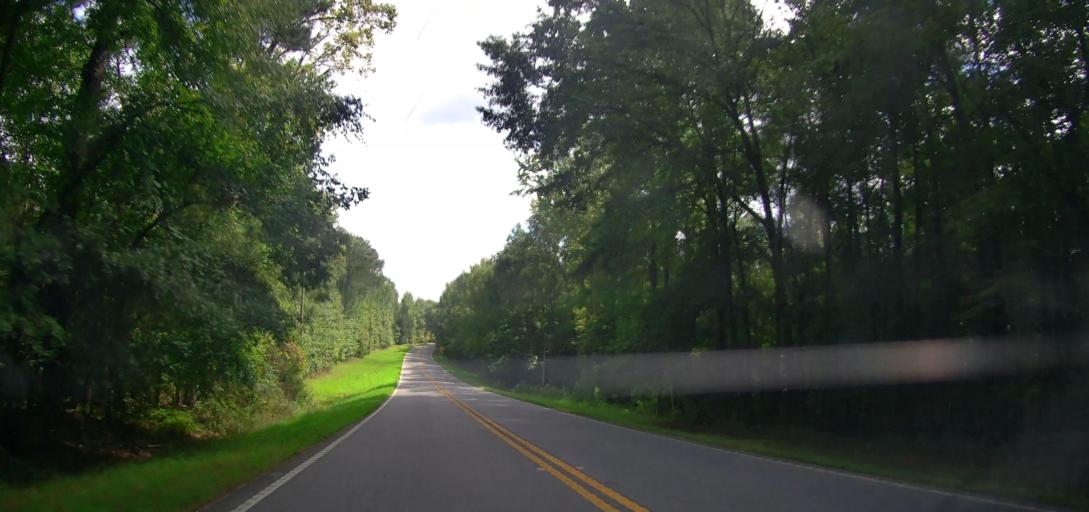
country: US
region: Georgia
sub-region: Talbot County
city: Talbotton
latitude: 32.6286
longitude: -84.4882
